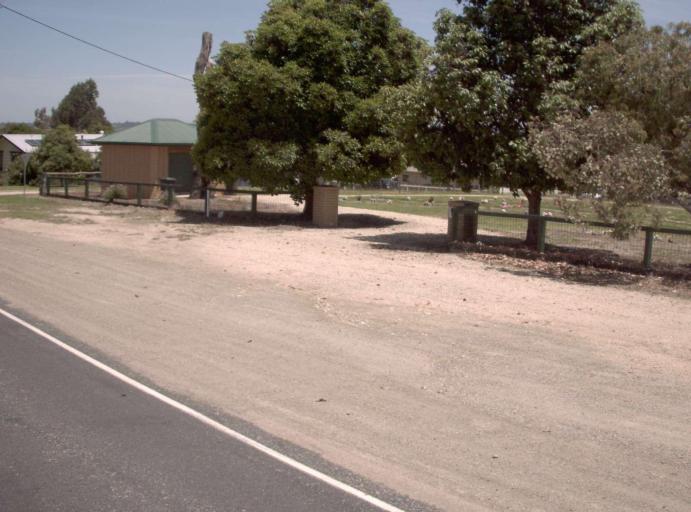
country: AU
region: Victoria
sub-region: East Gippsland
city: Lakes Entrance
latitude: -37.6979
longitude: 147.8366
